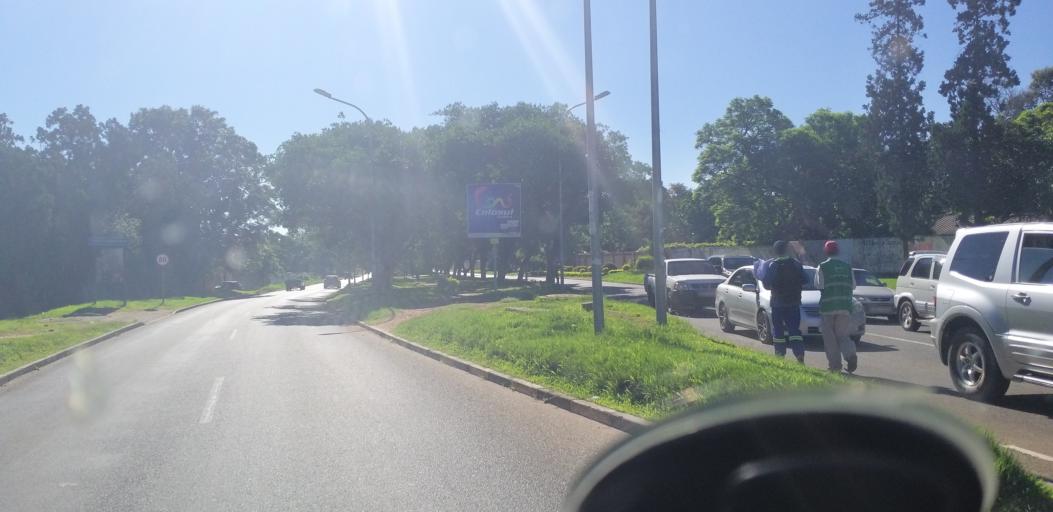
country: ZM
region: Lusaka
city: Lusaka
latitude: -15.4252
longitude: 28.3125
